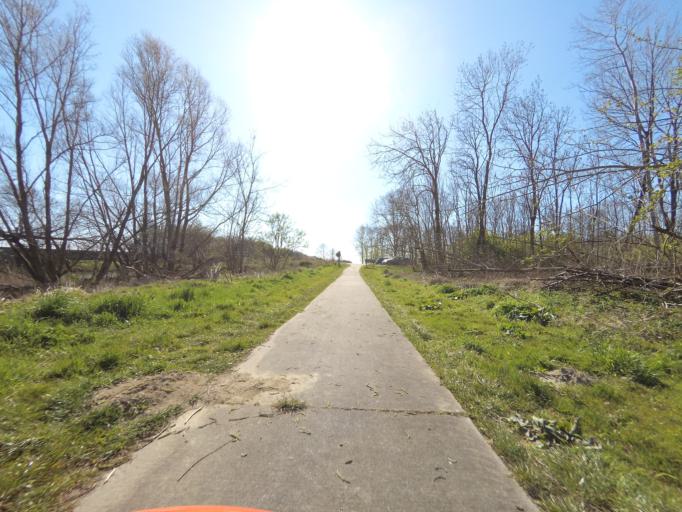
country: NL
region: Flevoland
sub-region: Gemeente Lelystad
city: Lelystad
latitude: 52.4255
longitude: 5.4202
